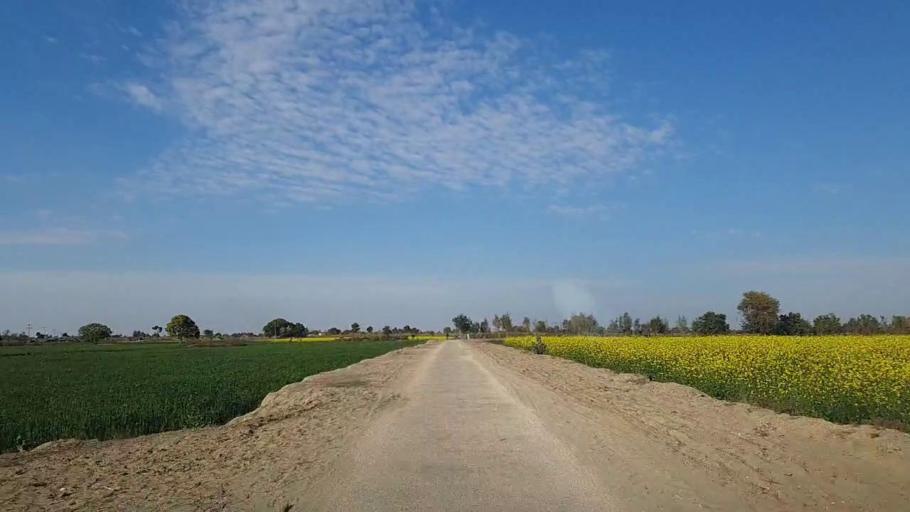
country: PK
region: Sindh
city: Khadro
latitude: 26.3064
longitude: 68.8343
